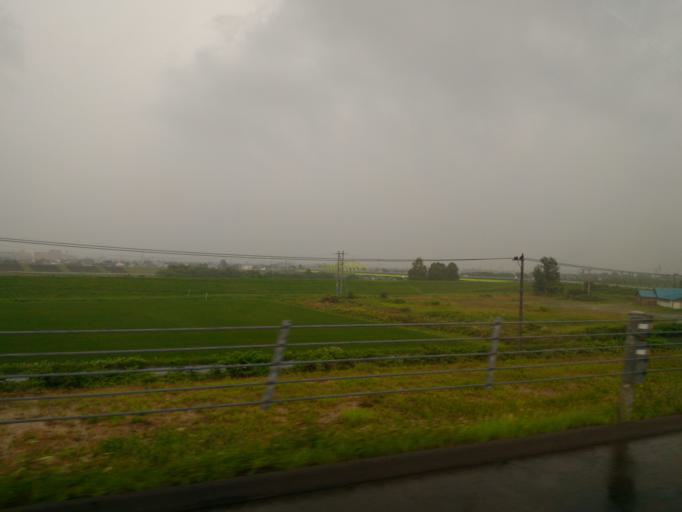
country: JP
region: Hokkaido
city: Nayoro
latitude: 44.3485
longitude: 142.4357
